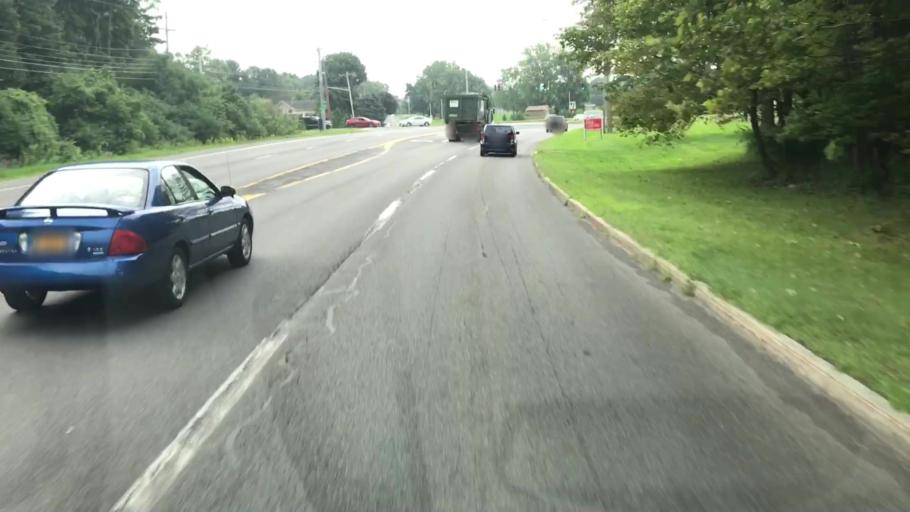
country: US
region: New York
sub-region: Onondaga County
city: Galeville
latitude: 43.1096
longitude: -76.1839
